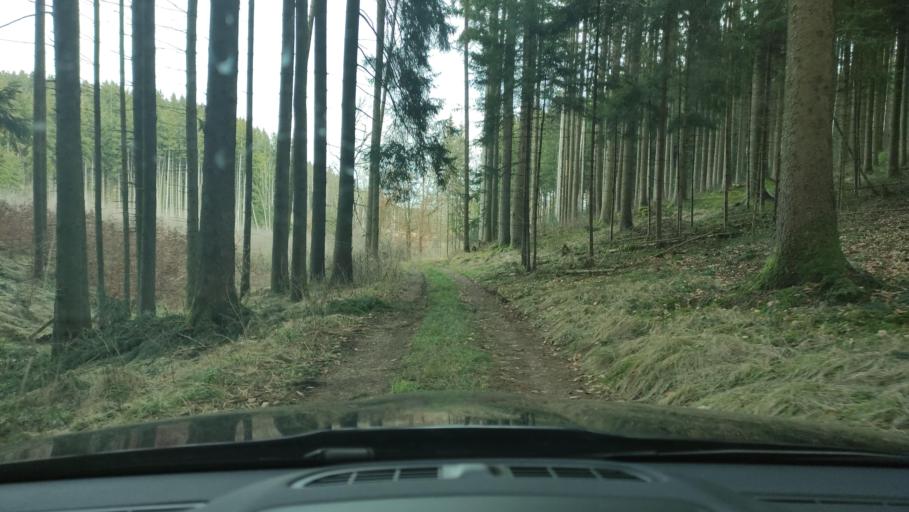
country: DE
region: Bavaria
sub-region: Swabia
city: Deisenhausen
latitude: 48.2558
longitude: 10.3455
